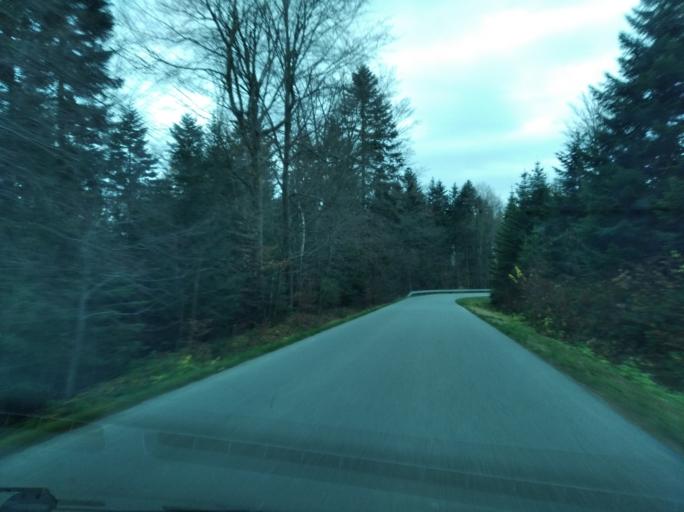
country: PL
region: Subcarpathian Voivodeship
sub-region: Powiat ropczycko-sedziszowski
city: Zagorzyce
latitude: 49.9617
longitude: 21.6915
